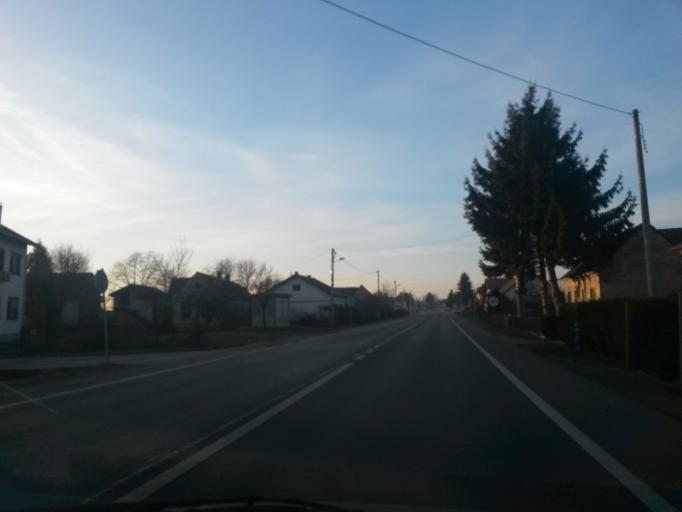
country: HR
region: Varazdinska
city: Jalzabet
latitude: 46.3011
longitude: 16.4782
